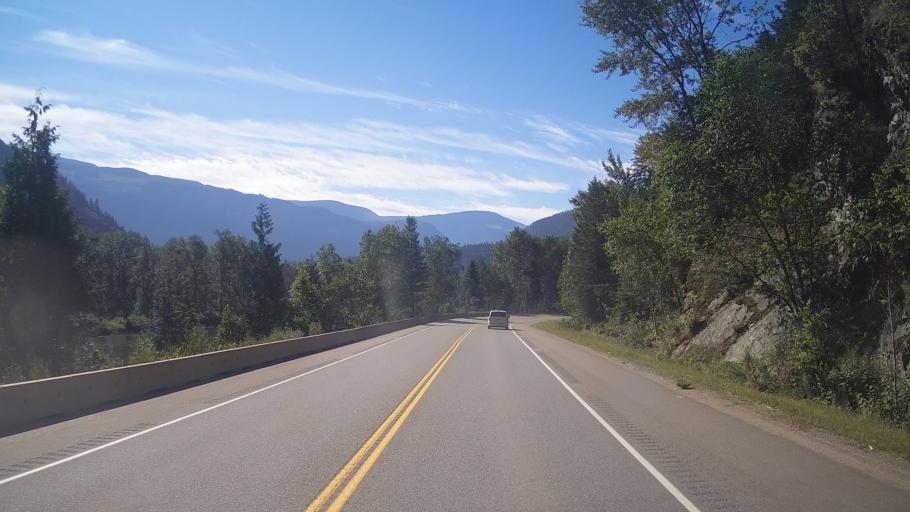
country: CA
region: British Columbia
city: Kamloops
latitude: 51.4754
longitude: -120.1802
